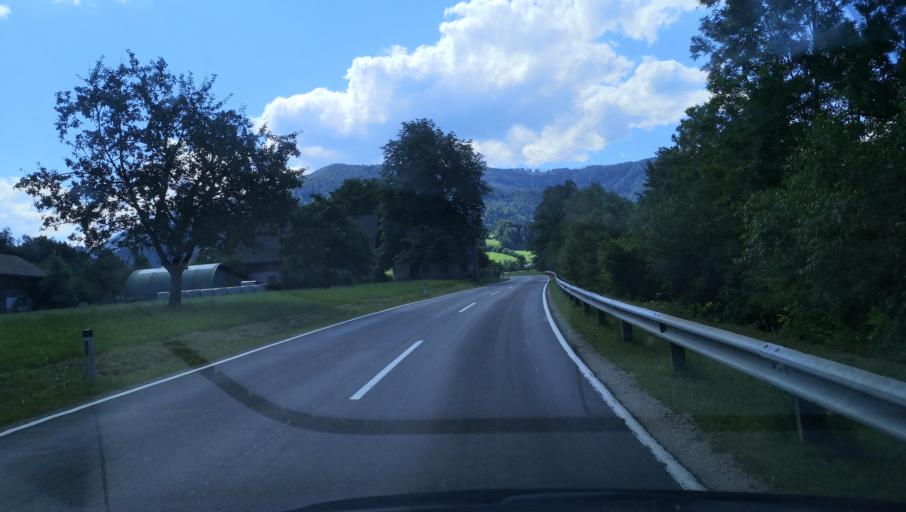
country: AT
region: Lower Austria
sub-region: Politischer Bezirk Scheibbs
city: Gresten
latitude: 47.9599
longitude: 15.0289
